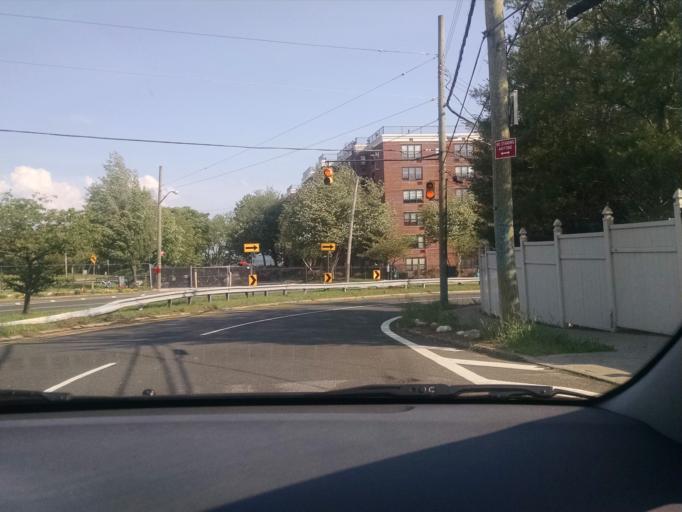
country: US
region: New York
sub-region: Kings County
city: Bensonhurst
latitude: 40.5967
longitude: -74.0620
